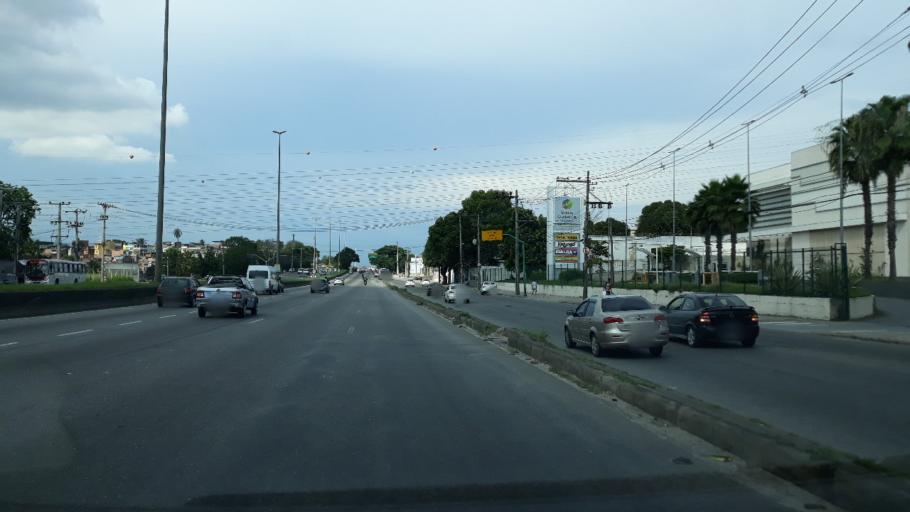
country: BR
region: Rio de Janeiro
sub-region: Sao Joao De Meriti
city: Sao Joao de Meriti
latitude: -22.8402
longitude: -43.3691
